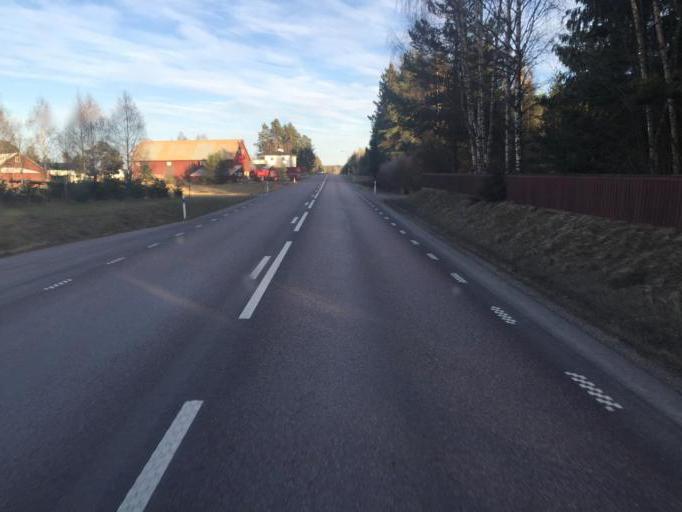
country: SE
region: Dalarna
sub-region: Borlange Kommun
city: Borlaenge
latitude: 60.5261
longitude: 15.3503
